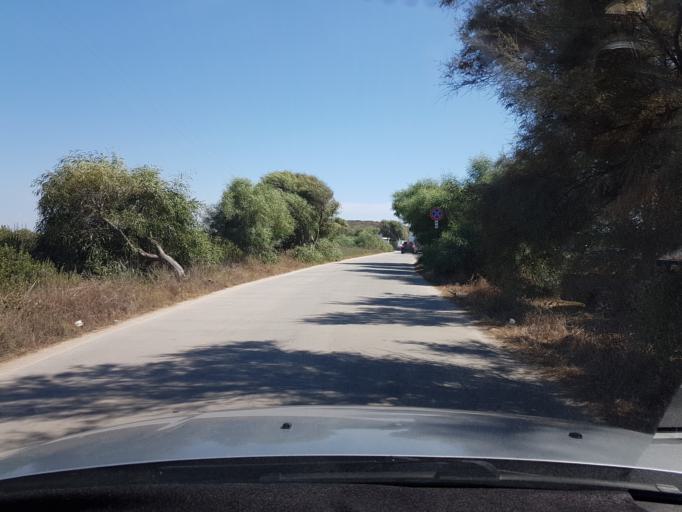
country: IT
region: Sardinia
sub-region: Provincia di Oristano
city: Cabras
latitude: 39.8829
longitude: 8.4392
